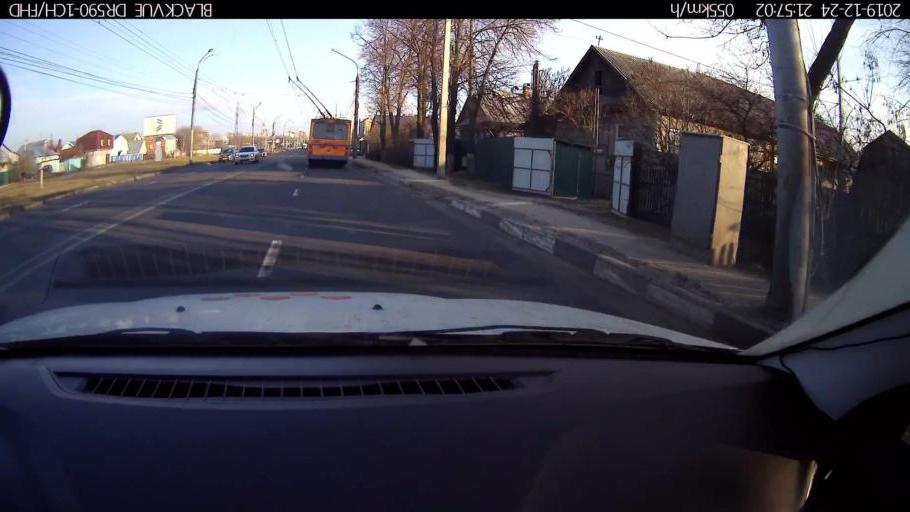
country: RU
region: Nizjnij Novgorod
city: Burevestnik
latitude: 56.2205
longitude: 43.8474
